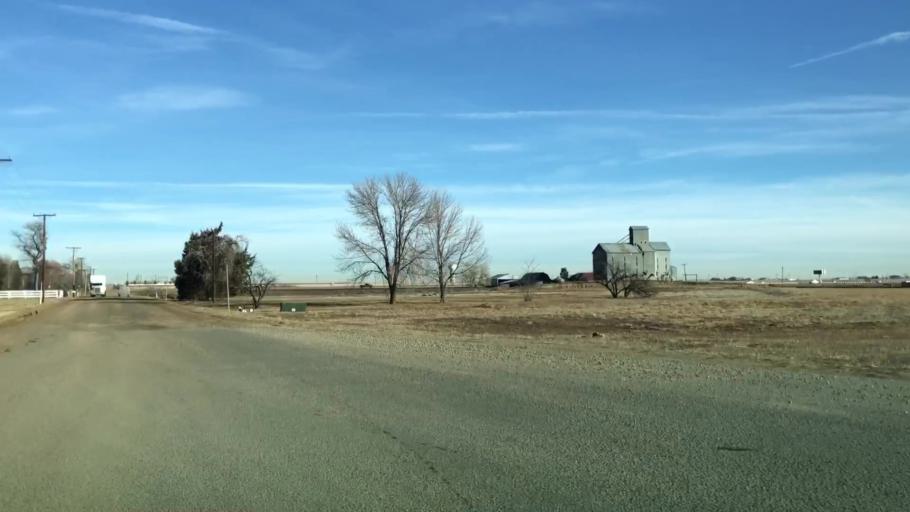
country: US
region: Colorado
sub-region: Weld County
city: Johnstown
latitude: 40.4037
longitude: -104.9643
